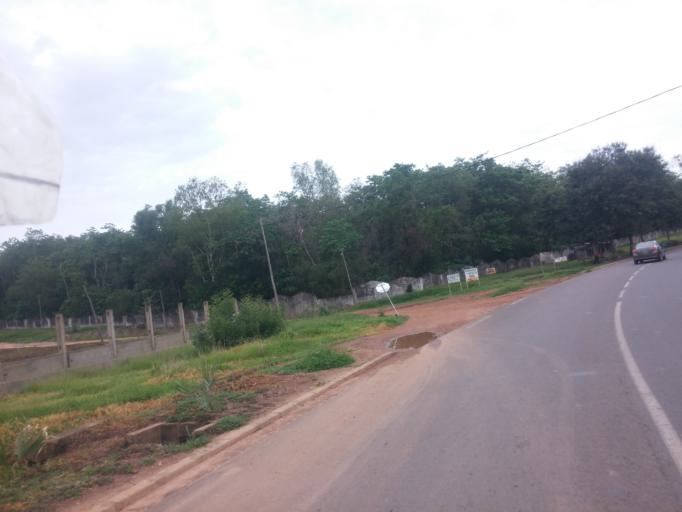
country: TG
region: Kara
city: Kara
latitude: 9.5493
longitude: 1.1802
